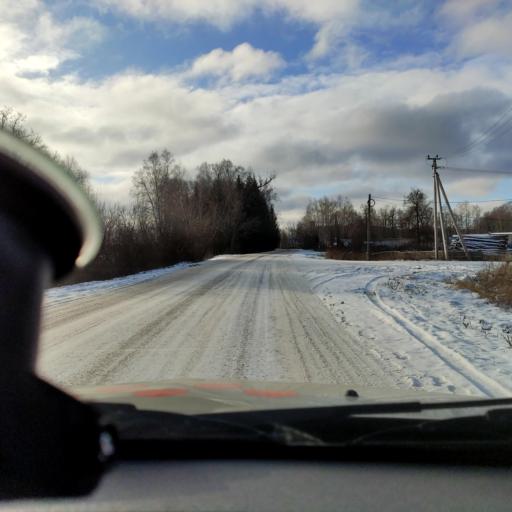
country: RU
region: Bashkortostan
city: Avdon
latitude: 54.7814
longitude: 55.7571
